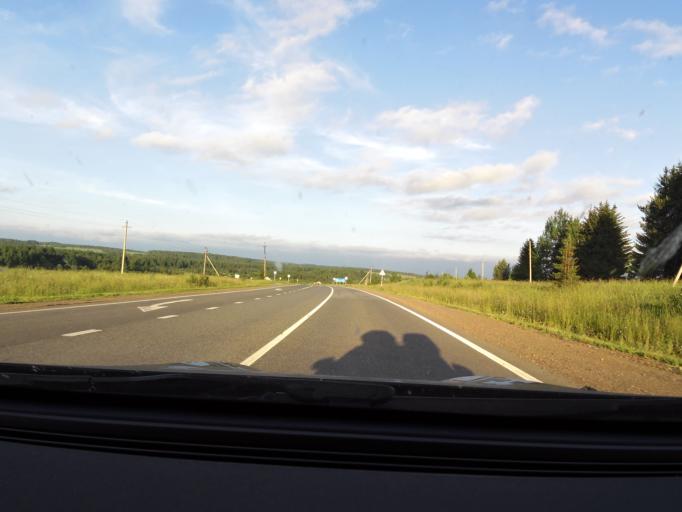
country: RU
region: Perm
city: Siva
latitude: 58.4856
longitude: 54.0690
